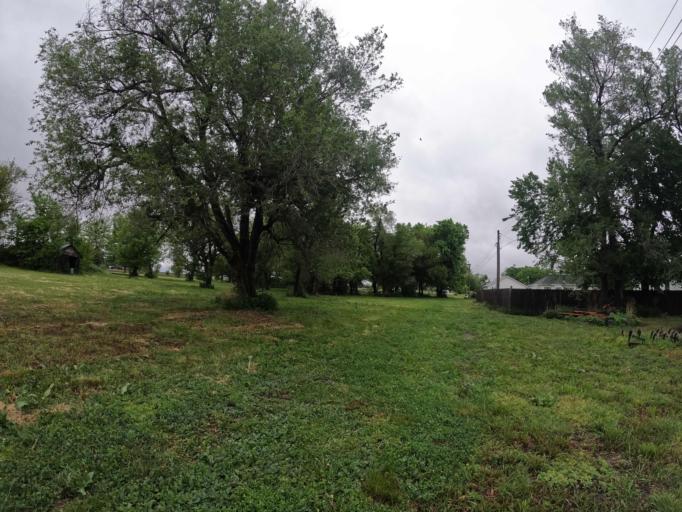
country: US
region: Nebraska
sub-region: Clay County
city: Harvard
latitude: 40.6249
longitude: -98.0992
